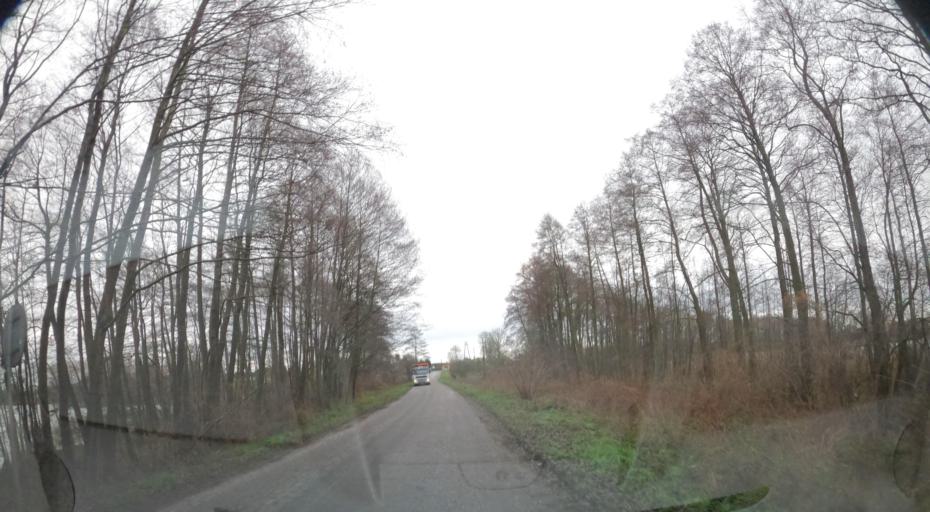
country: PL
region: Greater Poland Voivodeship
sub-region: Powiat pilski
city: Wysoka
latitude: 53.2571
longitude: 17.1179
